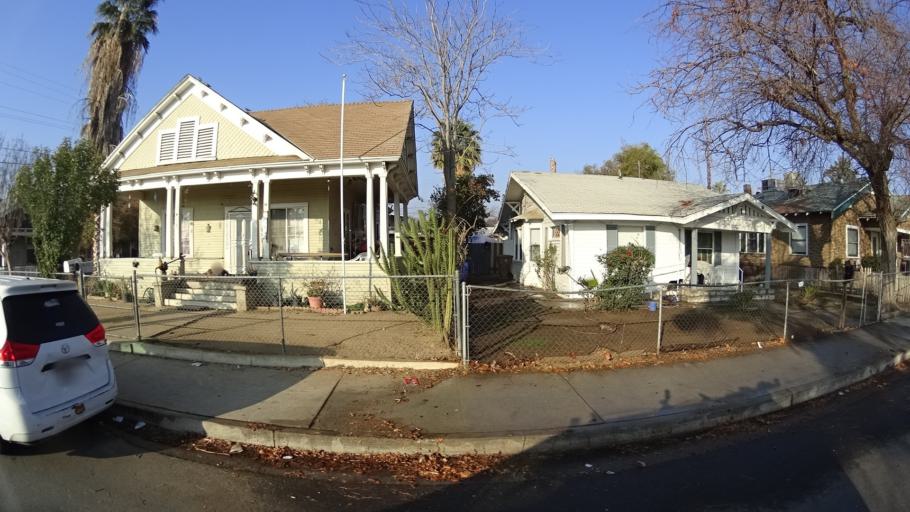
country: US
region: California
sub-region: Kern County
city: Bakersfield
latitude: 35.3842
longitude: -118.9870
